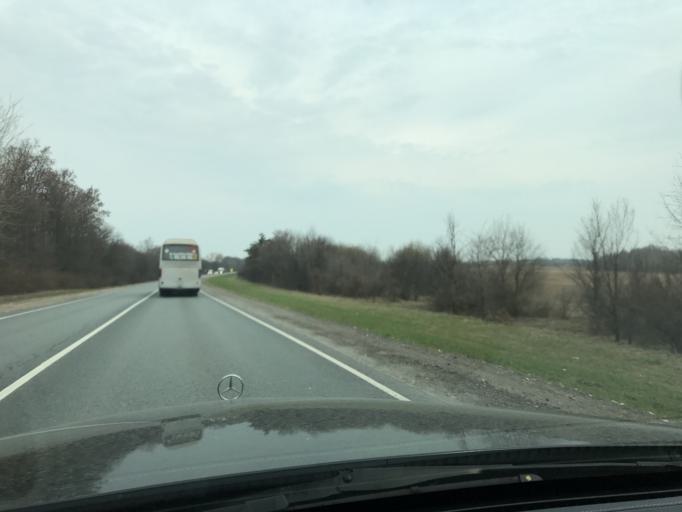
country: RU
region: Vladimir
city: Suzdal'
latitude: 56.3776
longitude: 40.4588
